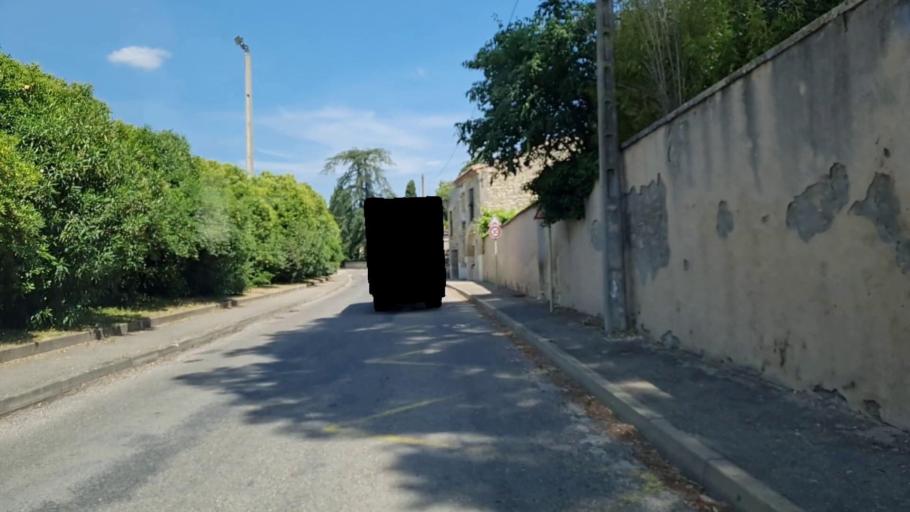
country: FR
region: Languedoc-Roussillon
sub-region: Departement du Gard
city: Saint-Gervasy
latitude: 43.8772
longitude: 4.4673
